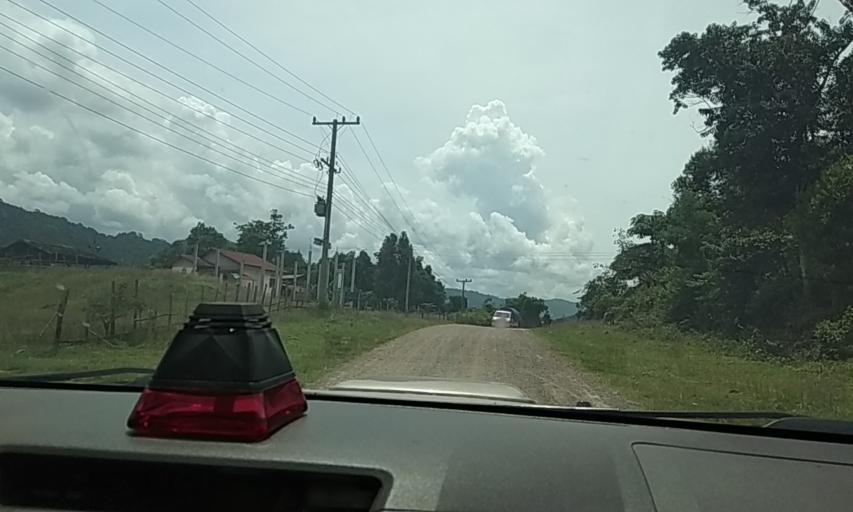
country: LA
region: Bolikhamxai
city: Ban Nahin
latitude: 18.1520
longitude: 104.7254
